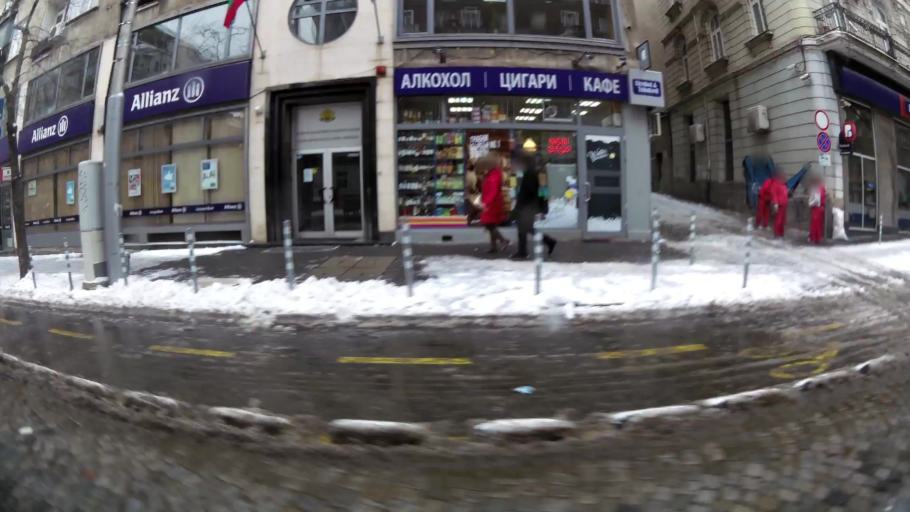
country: BG
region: Sofia-Capital
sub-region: Stolichna Obshtina
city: Sofia
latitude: 42.6980
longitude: 23.3266
